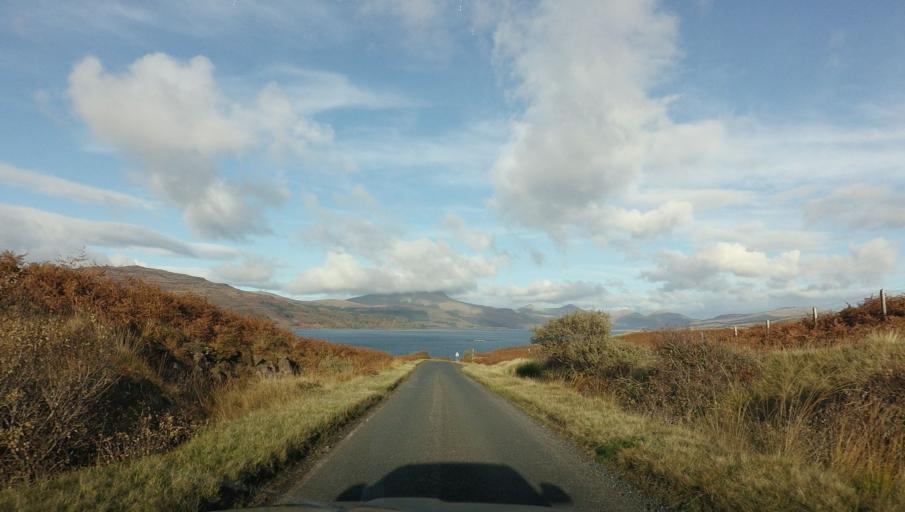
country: GB
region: Scotland
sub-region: Argyll and Bute
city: Isle Of Mull
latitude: 56.3424
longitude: -6.1233
